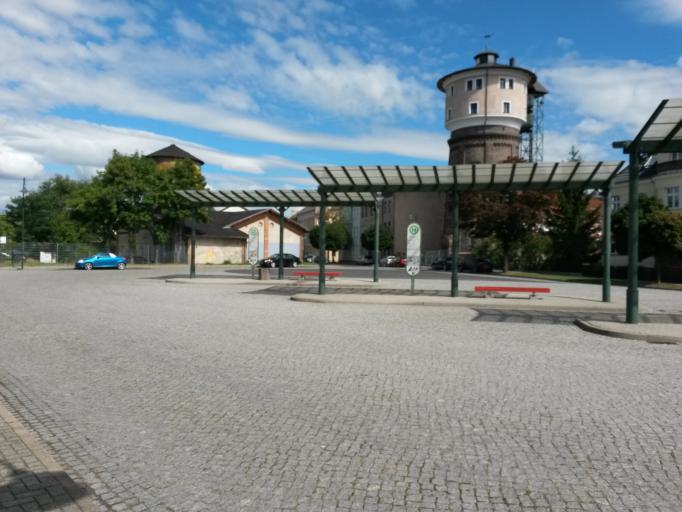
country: DE
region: Brandenburg
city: Angermunde
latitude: 53.0156
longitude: 13.9969
